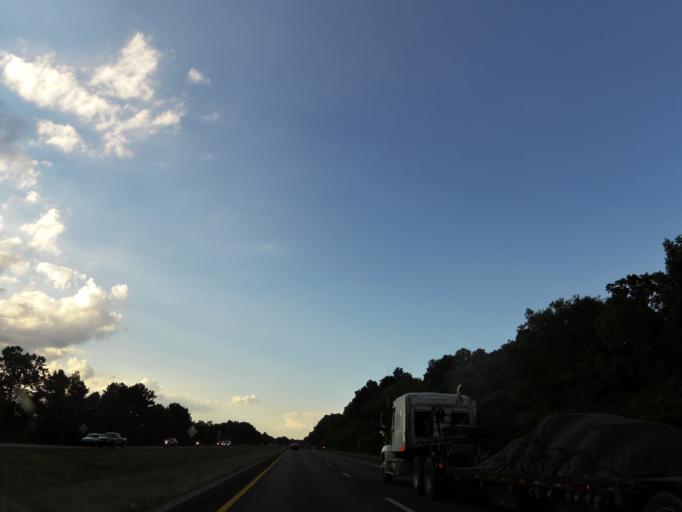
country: US
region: Tennessee
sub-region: Williamson County
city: Thompson's Station
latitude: 35.7686
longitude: -86.8645
